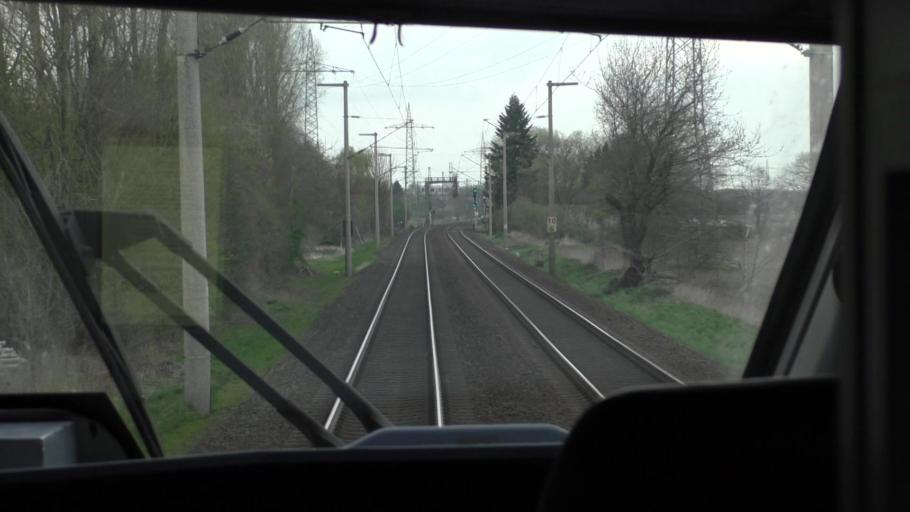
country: DE
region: North Rhine-Westphalia
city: Bruhl
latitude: 50.8631
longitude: 6.9086
